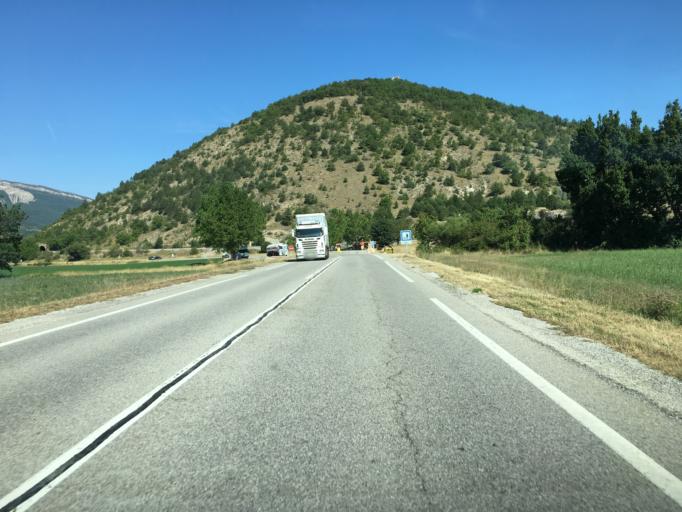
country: FR
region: Provence-Alpes-Cote d'Azur
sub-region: Departement des Hautes-Alpes
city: Serres
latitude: 44.3762
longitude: 5.7495
